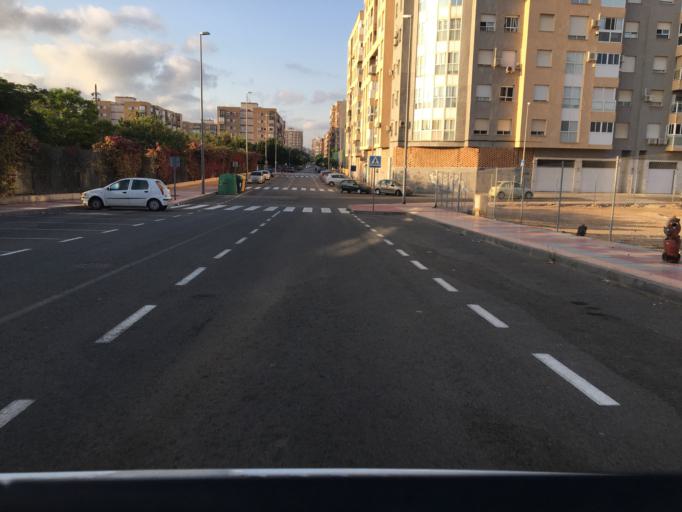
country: ES
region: Murcia
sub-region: Murcia
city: Cartagena
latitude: 37.6201
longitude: -0.9928
